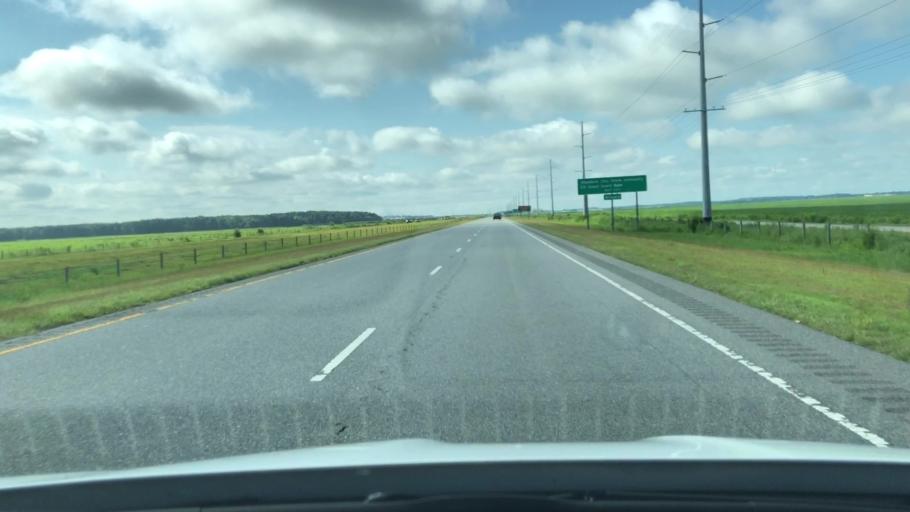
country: US
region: North Carolina
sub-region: Pasquotank County
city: Elizabeth City
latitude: 36.3150
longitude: -76.3081
